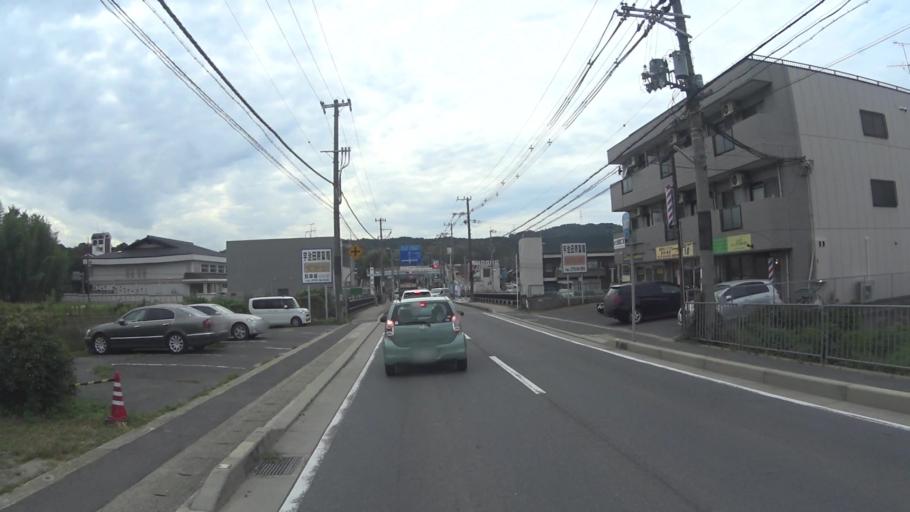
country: JP
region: Kyoto
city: Uji
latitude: 34.8502
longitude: 135.8547
